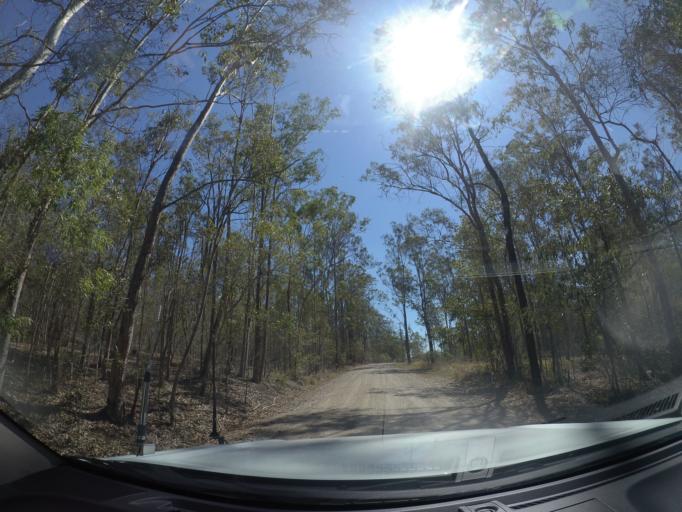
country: AU
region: Queensland
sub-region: Ipswich
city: Springfield Lakes
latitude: -27.7438
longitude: 152.9371
